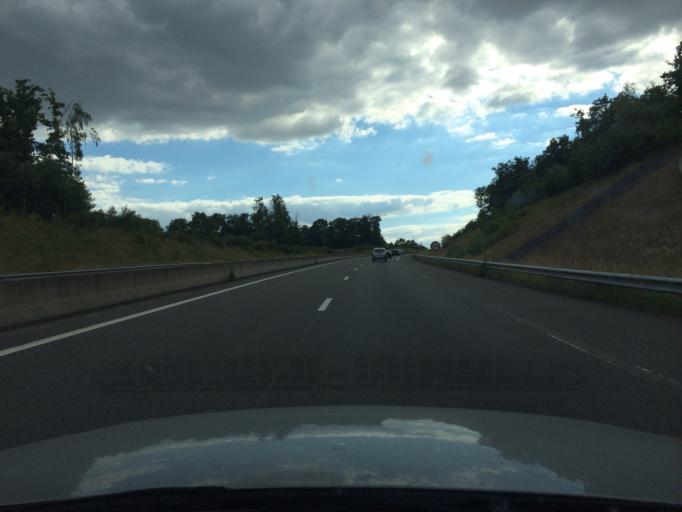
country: FR
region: Lorraine
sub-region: Departement de la Moselle
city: Lorquin
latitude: 48.5994
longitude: 6.8402
